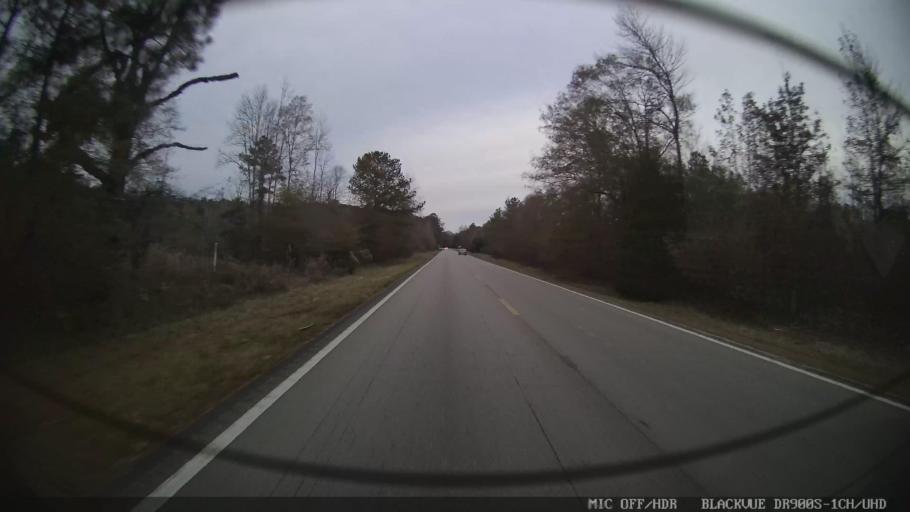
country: US
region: Mississippi
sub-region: Clarke County
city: Stonewall
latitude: 32.0364
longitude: -88.8760
